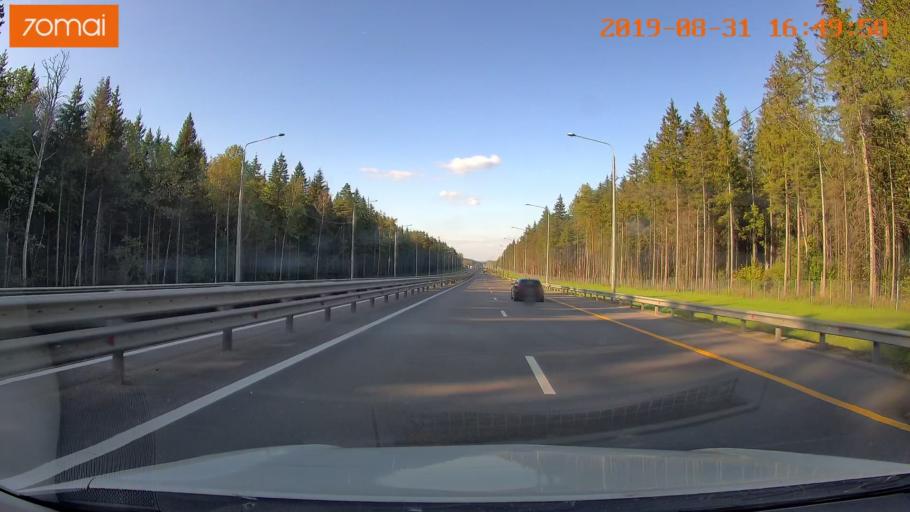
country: RU
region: Kaluga
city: Pyatovskiy
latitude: 54.7002
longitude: 36.1590
